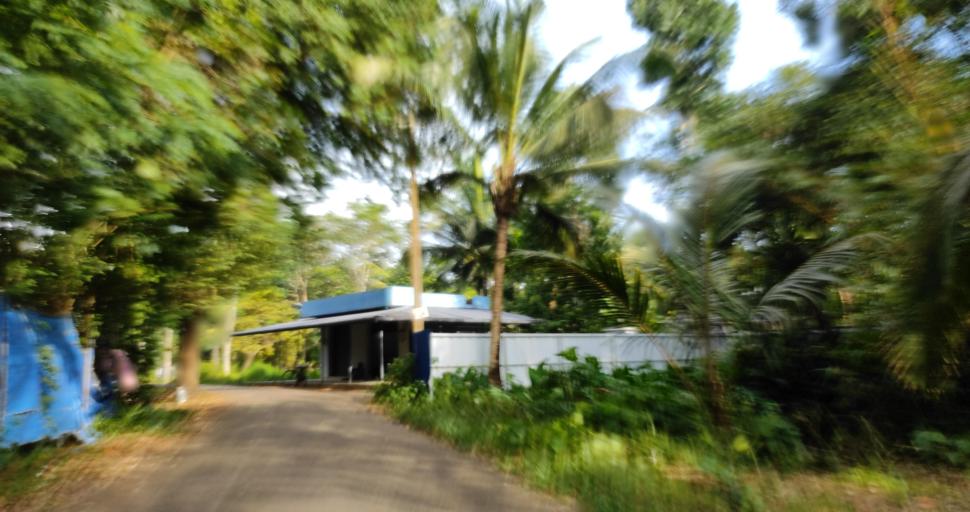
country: IN
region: Kerala
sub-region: Alappuzha
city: Shertallai
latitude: 9.6154
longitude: 76.3429
